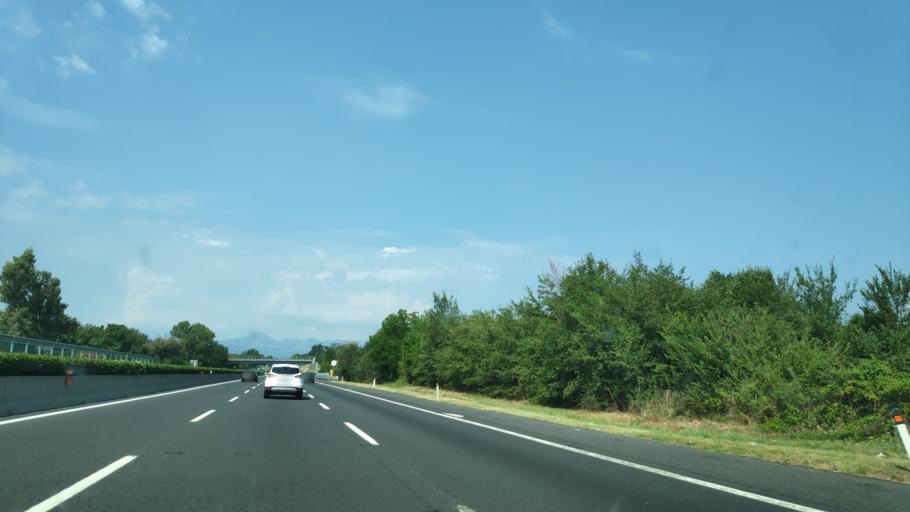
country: IT
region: Latium
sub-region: Provincia di Frosinone
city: Pofi
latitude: 41.5550
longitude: 13.4300
